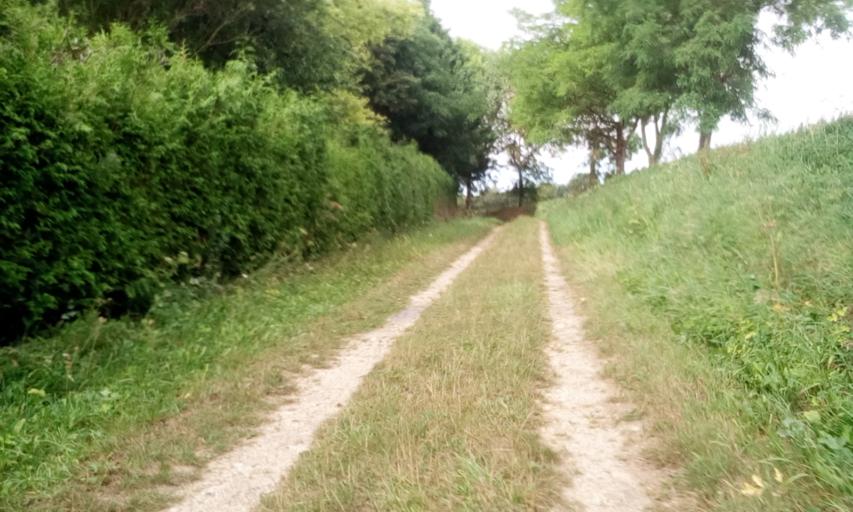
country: FR
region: Lower Normandy
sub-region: Departement du Calvados
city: Tilly-sur-Seulles
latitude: 49.2236
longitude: -0.6233
